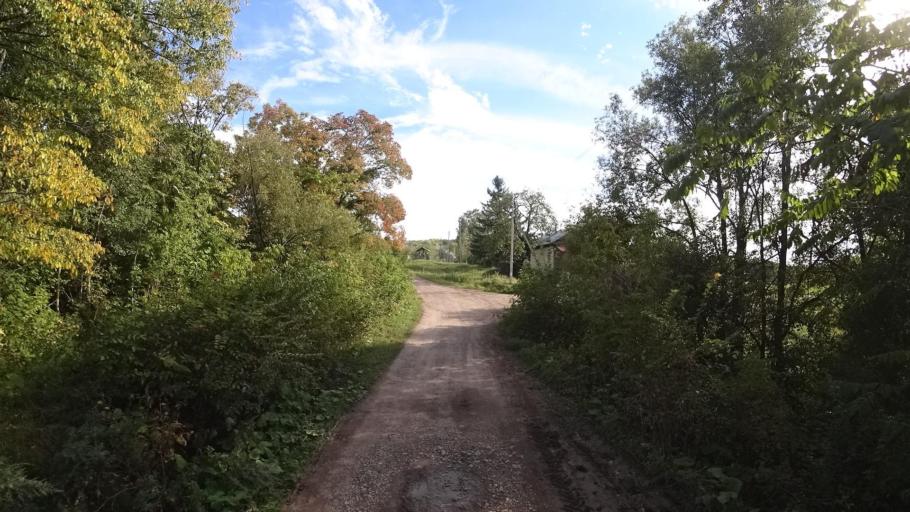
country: RU
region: Primorskiy
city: Dostoyevka
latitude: 44.2939
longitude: 133.4485
